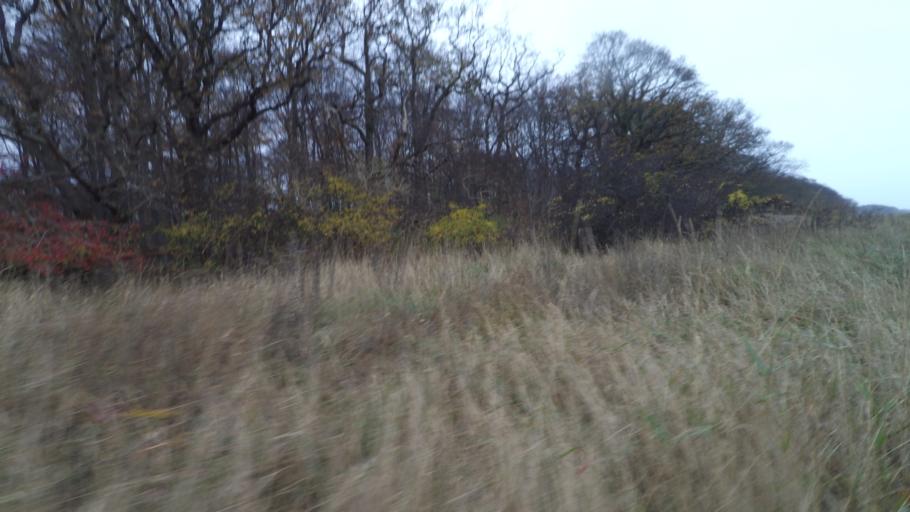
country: DK
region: Central Jutland
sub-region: Odder Kommune
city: Odder
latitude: 55.9015
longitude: 10.2283
